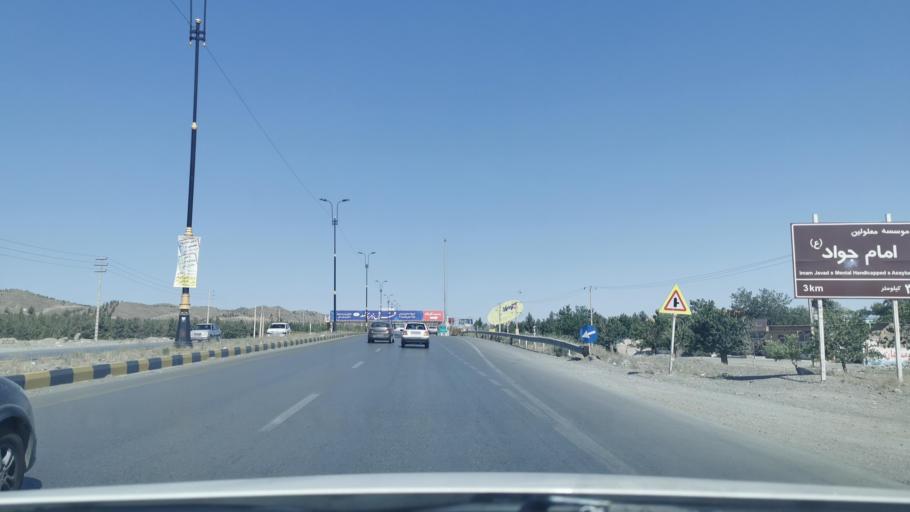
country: IR
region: Razavi Khorasan
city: Torqabeh
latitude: 36.4033
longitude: 59.3841
